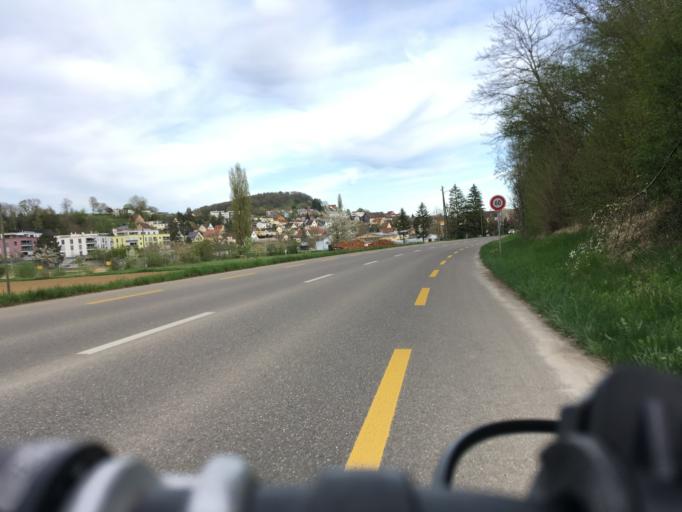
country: CH
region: Schaffhausen
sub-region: Bezirk Reiat
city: Thayngen
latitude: 47.7528
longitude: 8.7006
